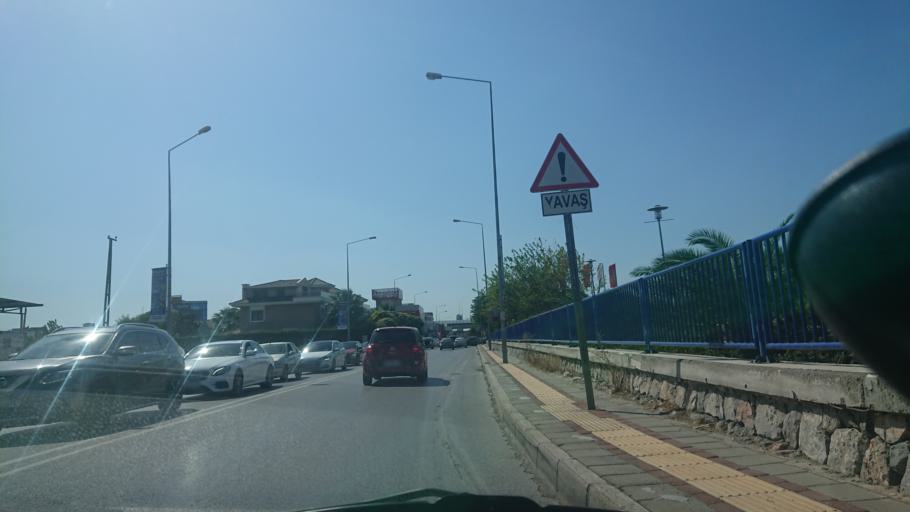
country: TR
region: Izmir
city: Bornova
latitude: 38.4489
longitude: 27.2109
